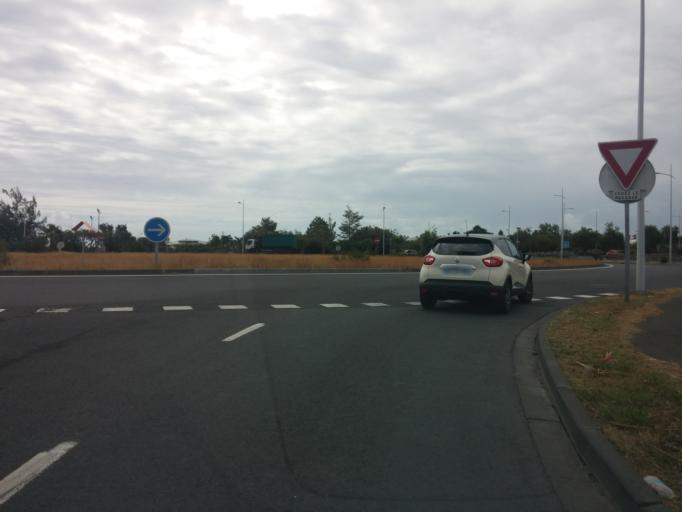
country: RE
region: Reunion
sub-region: Reunion
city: Le Port
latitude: -20.9532
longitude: 55.2945
